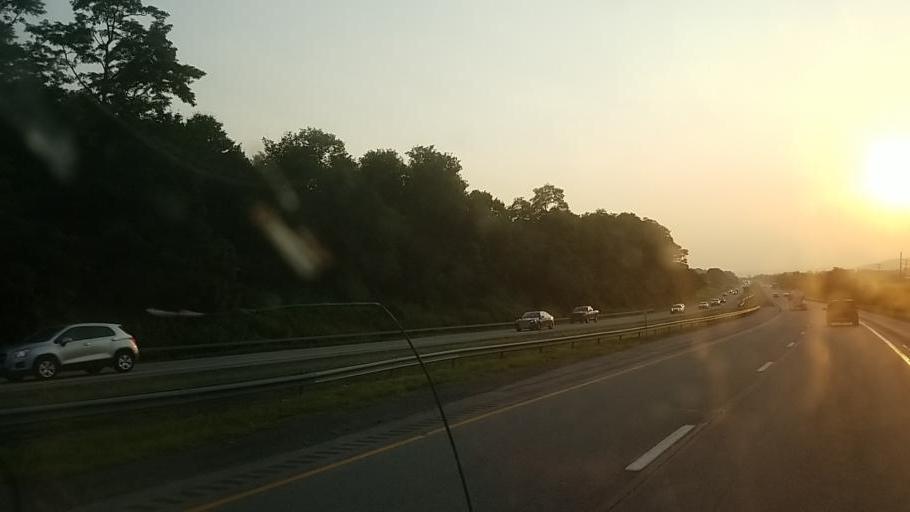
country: US
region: New York
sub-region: Herkimer County
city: Herkimer
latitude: 43.0137
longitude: -74.9263
